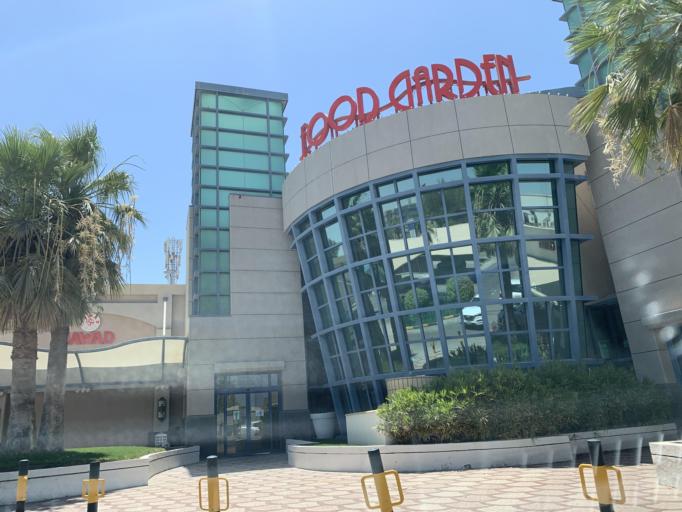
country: BH
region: Manama
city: Jidd Hafs
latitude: 26.2215
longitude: 50.4895
